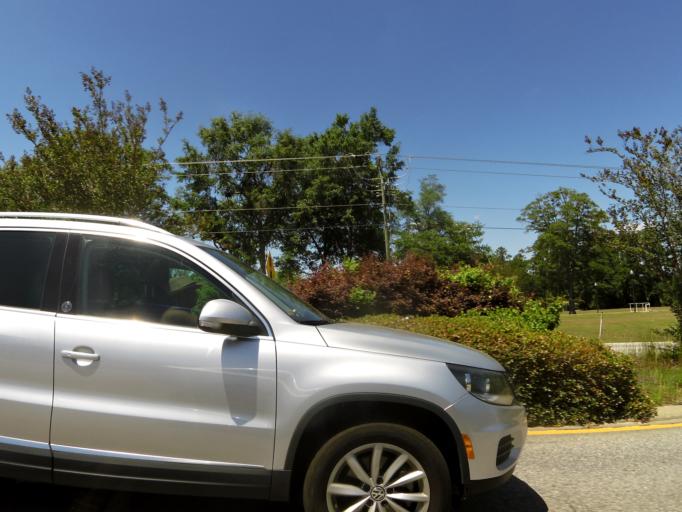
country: US
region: South Carolina
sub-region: Aiken County
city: Clearwater
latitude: 33.5046
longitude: -81.8969
